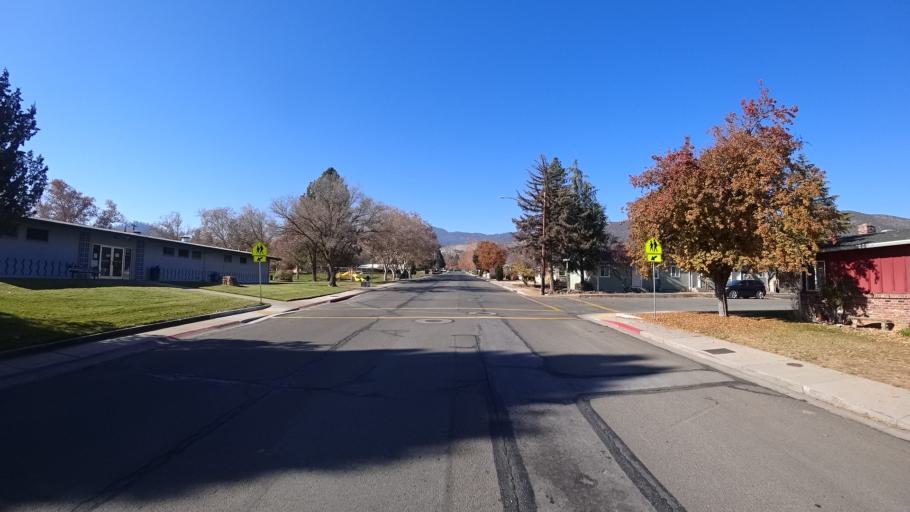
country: US
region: California
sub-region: Siskiyou County
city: Yreka
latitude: 41.7392
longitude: -122.6394
